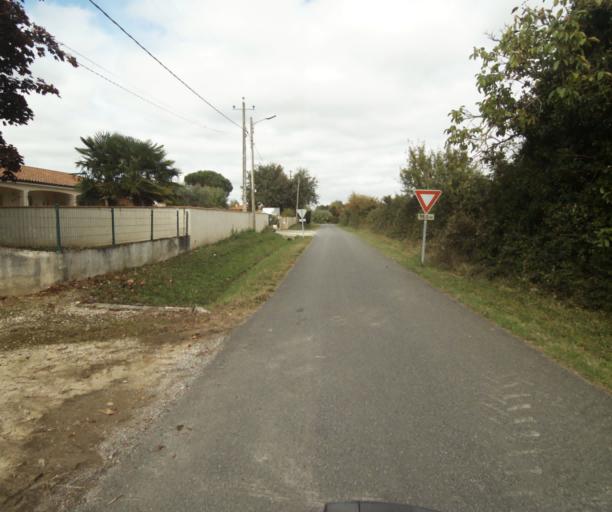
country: FR
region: Midi-Pyrenees
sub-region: Departement du Tarn-et-Garonne
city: Montech
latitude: 43.9566
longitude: 1.2234
